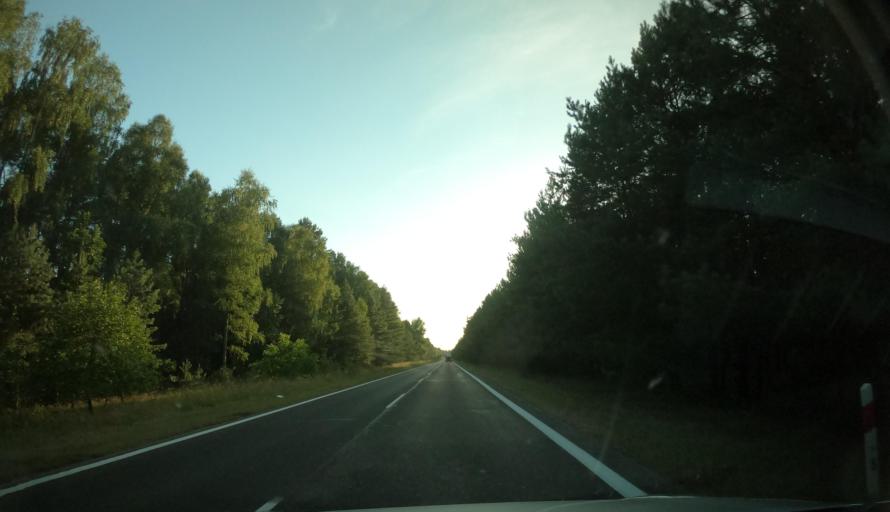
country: PL
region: Kujawsko-Pomorskie
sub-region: Powiat bydgoski
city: Koronowo
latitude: 53.3115
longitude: 18.0037
